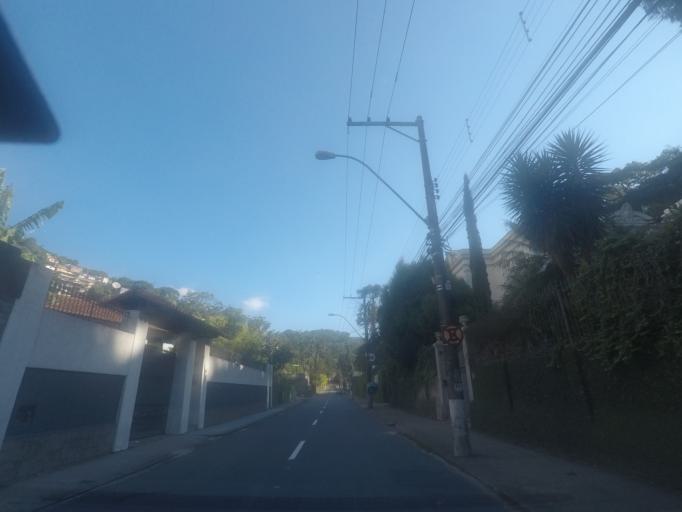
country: BR
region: Rio de Janeiro
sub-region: Petropolis
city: Petropolis
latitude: -22.5107
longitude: -43.1671
